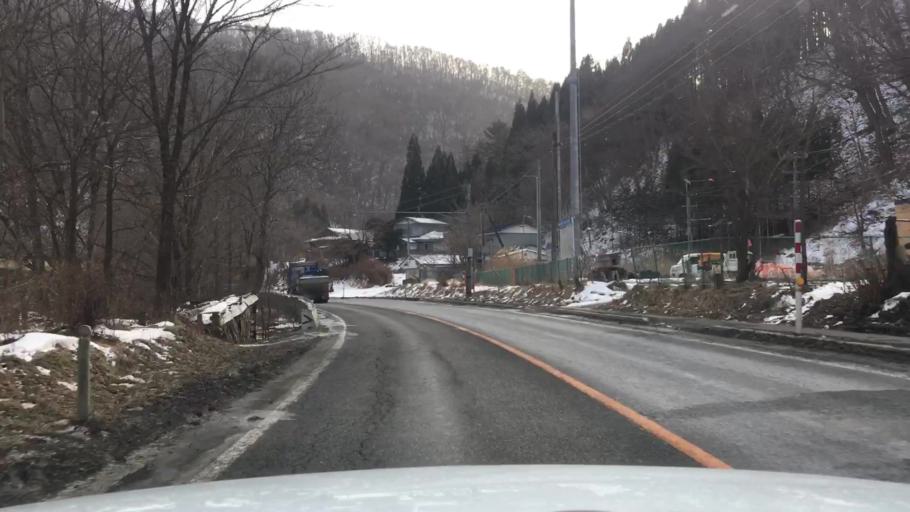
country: JP
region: Iwate
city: Tono
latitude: 39.6262
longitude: 141.5138
